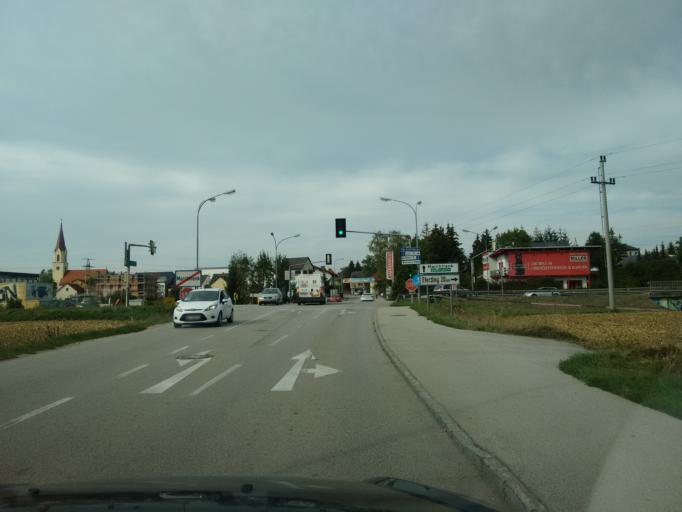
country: AT
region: Upper Austria
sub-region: Wels-Land
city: Marchtrenk
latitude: 48.1884
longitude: 14.1108
